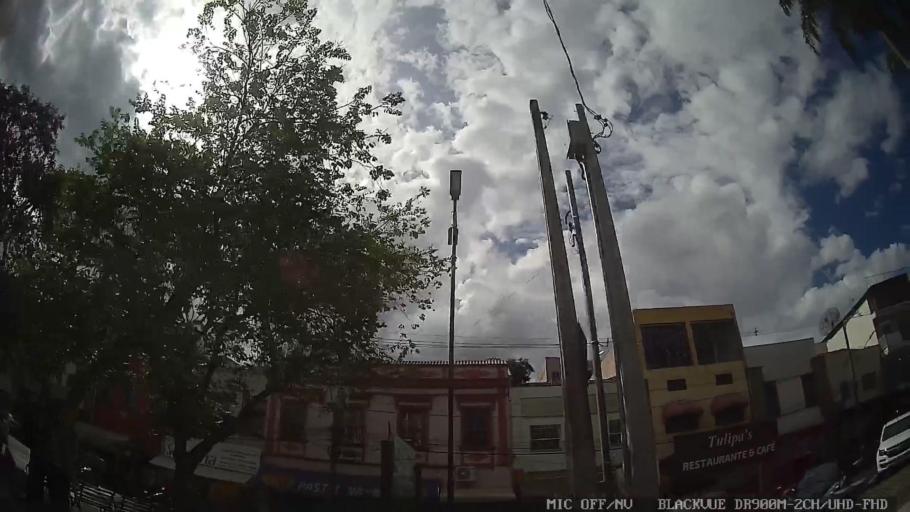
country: BR
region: Sao Paulo
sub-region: Pedreira
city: Pedreira
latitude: -22.7423
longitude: -46.9116
